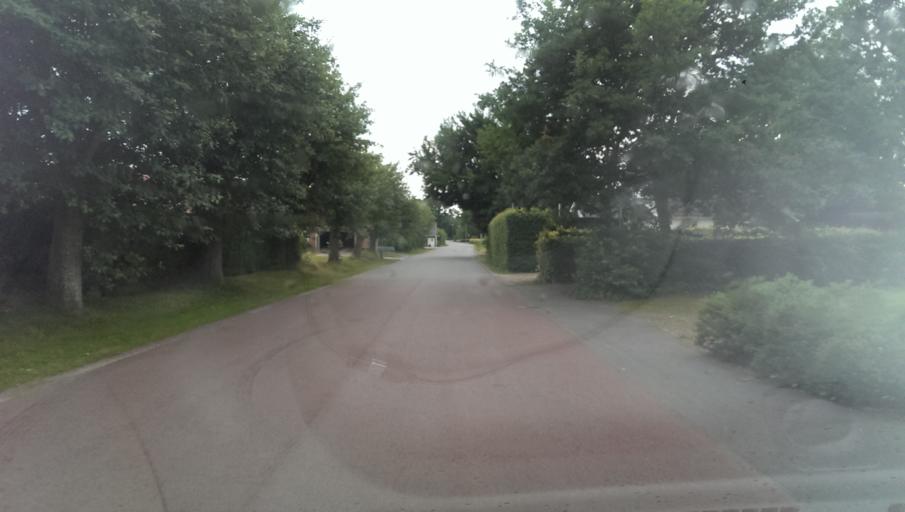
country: DK
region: South Denmark
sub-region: Esbjerg Kommune
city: Bramming
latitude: 55.4354
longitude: 8.7196
